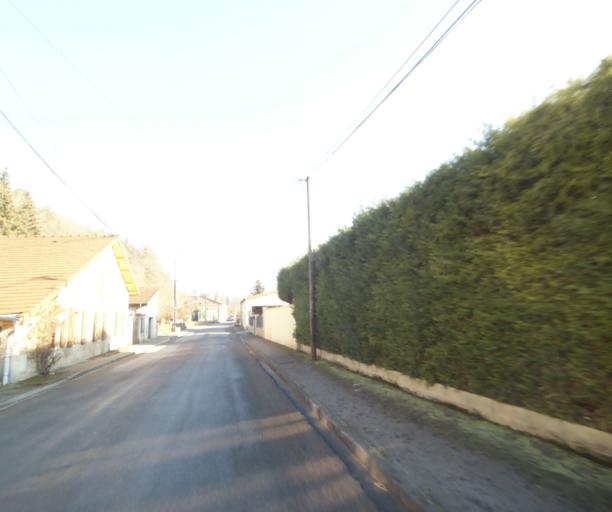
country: FR
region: Champagne-Ardenne
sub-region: Departement de la Haute-Marne
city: Chevillon
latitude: 48.5273
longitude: 5.1463
